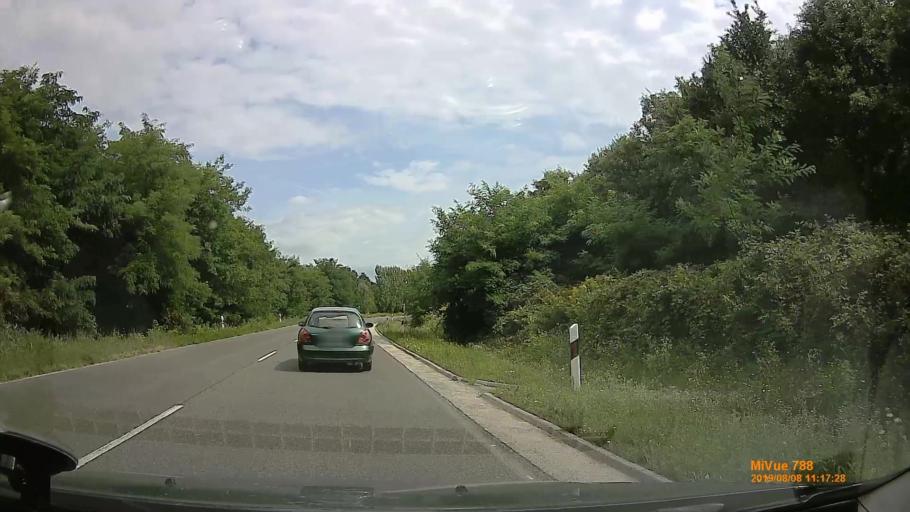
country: HU
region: Somogy
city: Balatonbereny
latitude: 46.6591
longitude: 17.3175
